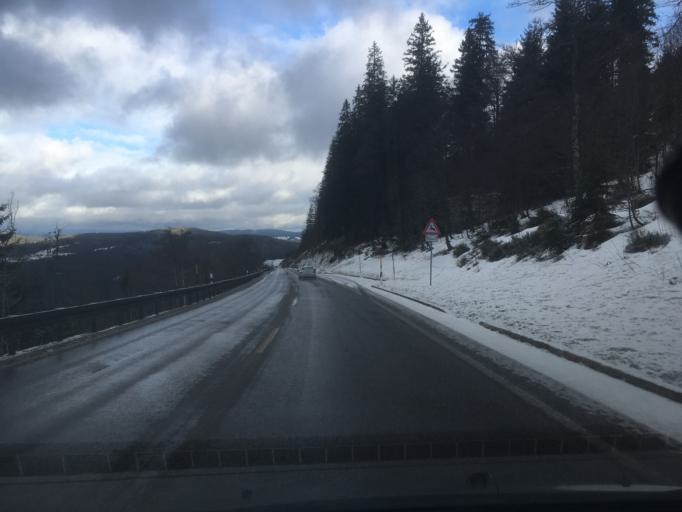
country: DE
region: Baden-Wuerttemberg
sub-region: Freiburg Region
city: Bernau
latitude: 47.8595
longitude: 8.0540
